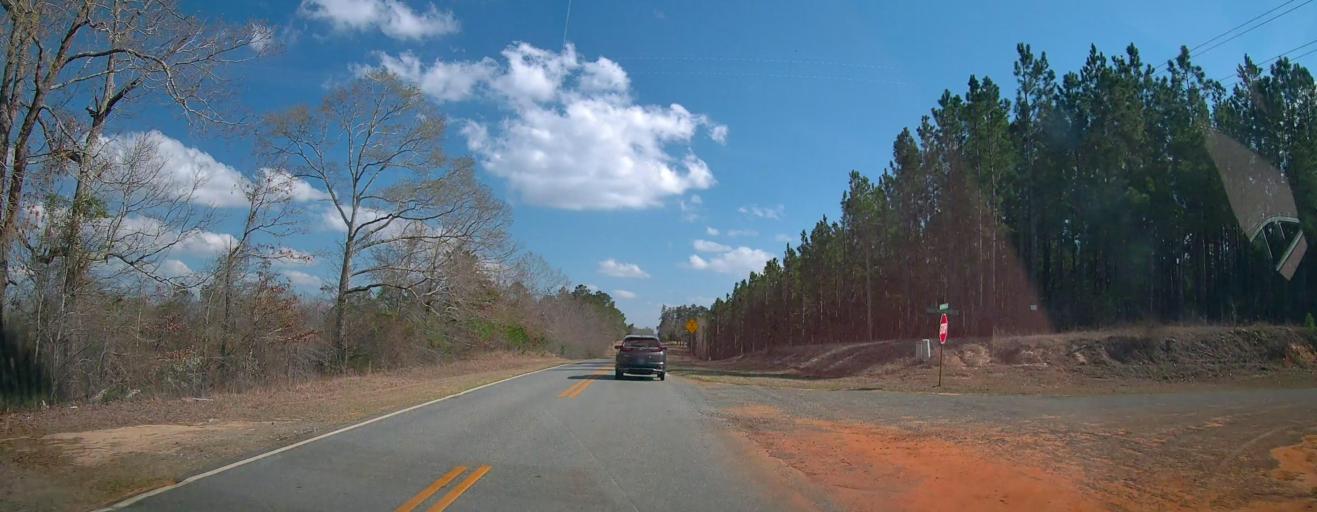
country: US
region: Georgia
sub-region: Laurens County
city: Dublin
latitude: 32.6221
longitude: -83.0897
